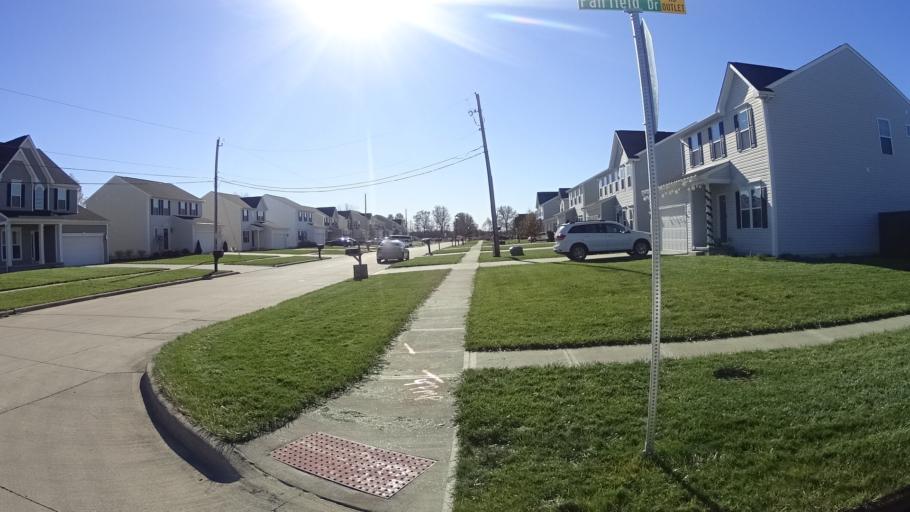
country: US
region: Ohio
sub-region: Lorain County
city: Elyria
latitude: 41.3644
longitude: -82.1656
